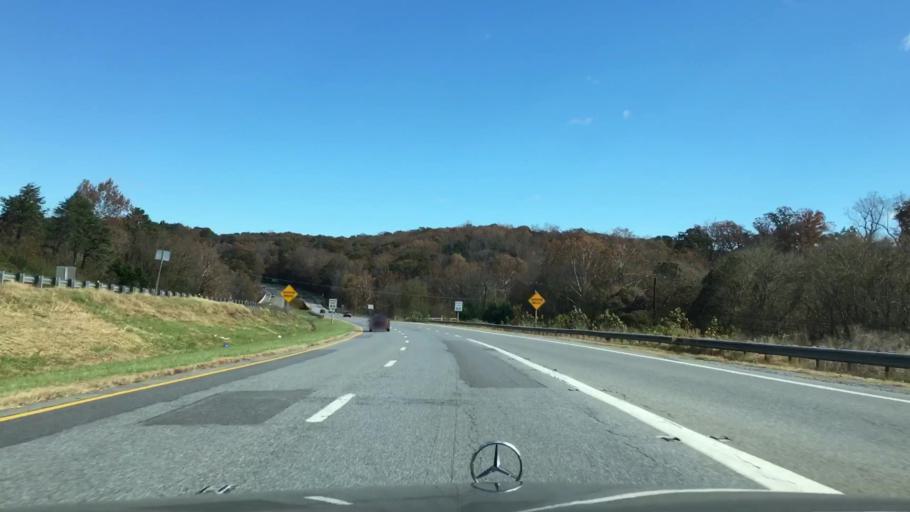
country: US
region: Virginia
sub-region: Campbell County
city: Altavista
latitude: 37.1384
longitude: -79.2472
